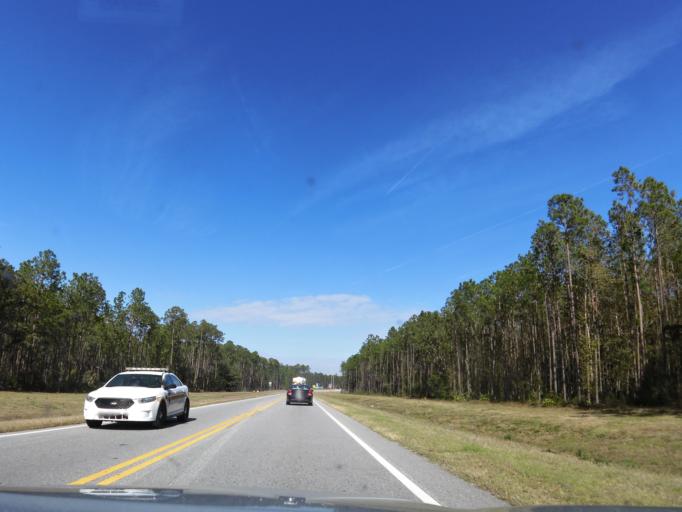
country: US
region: Georgia
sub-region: McIntosh County
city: Darien
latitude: 31.3008
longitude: -81.4840
